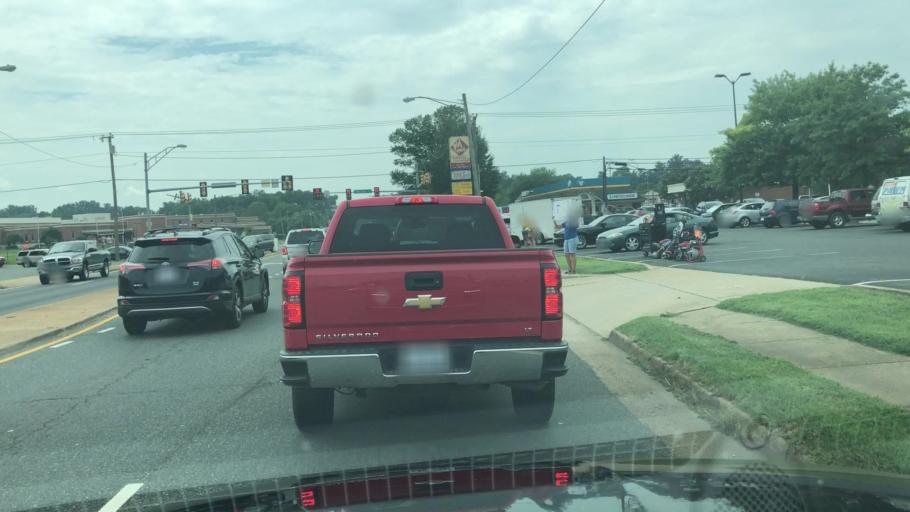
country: US
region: Virginia
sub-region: Stafford County
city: Falmouth
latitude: 38.3150
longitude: -77.4744
